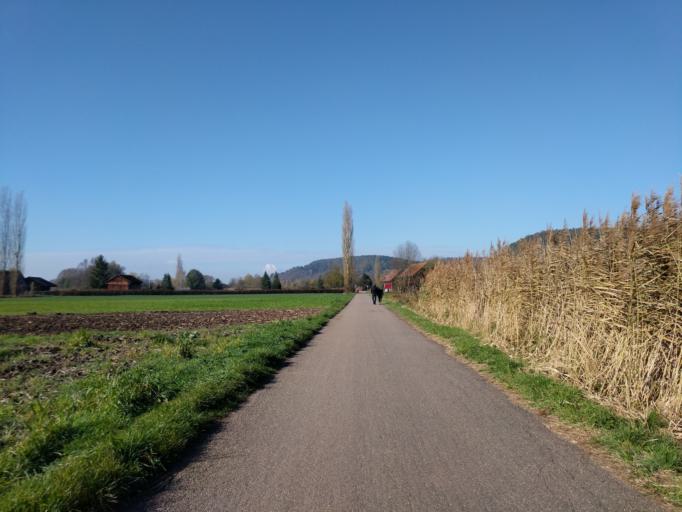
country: DE
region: Baden-Wuerttemberg
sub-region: Tuebingen Region
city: Tuebingen
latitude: 48.5217
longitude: 9.0268
